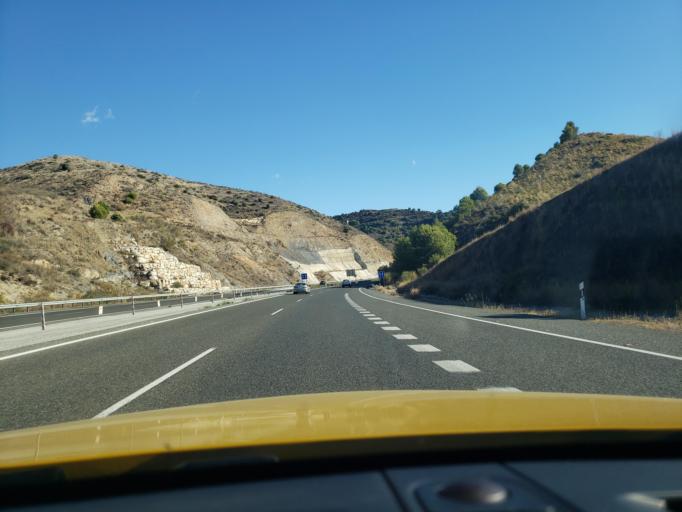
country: ES
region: Andalusia
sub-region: Provincia de Malaga
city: Marbella
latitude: 36.5235
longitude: -4.8567
